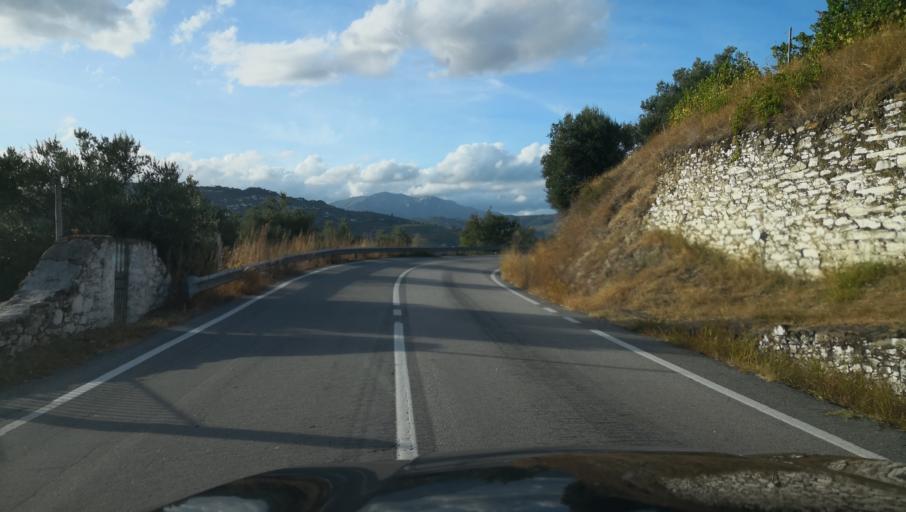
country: PT
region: Vila Real
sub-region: Peso da Regua
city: Peso da Regua
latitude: 41.1708
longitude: -7.7768
